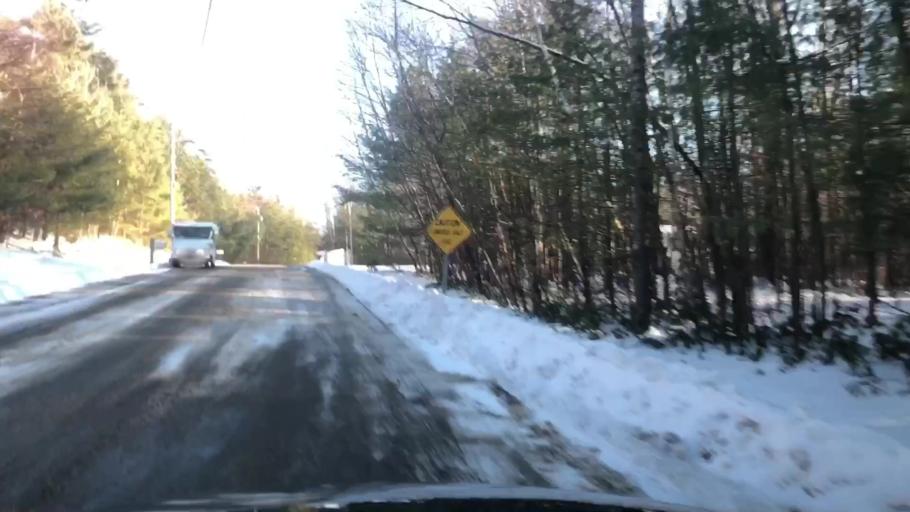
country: US
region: New Hampshire
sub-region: Hillsborough County
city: Milford
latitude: 42.8019
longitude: -71.6706
